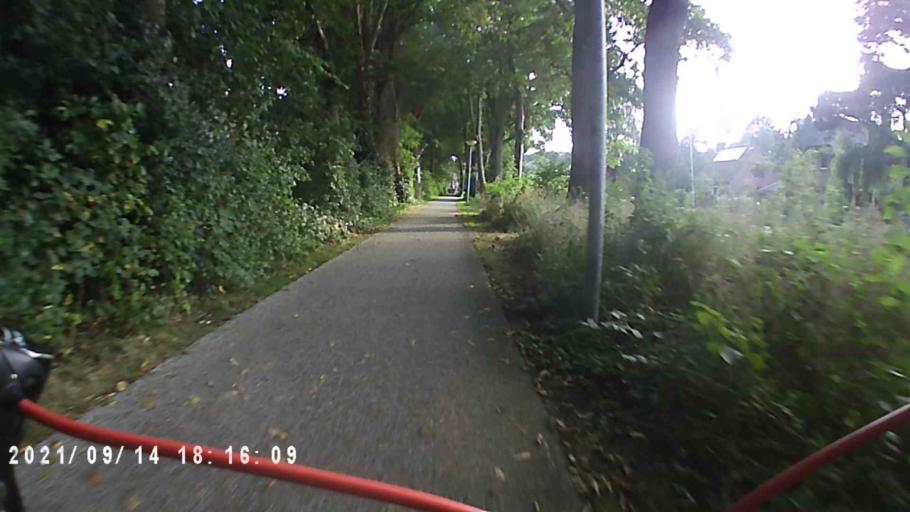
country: NL
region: Drenthe
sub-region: Gemeente Tynaarlo
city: Zuidlaren
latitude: 53.0826
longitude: 6.6706
